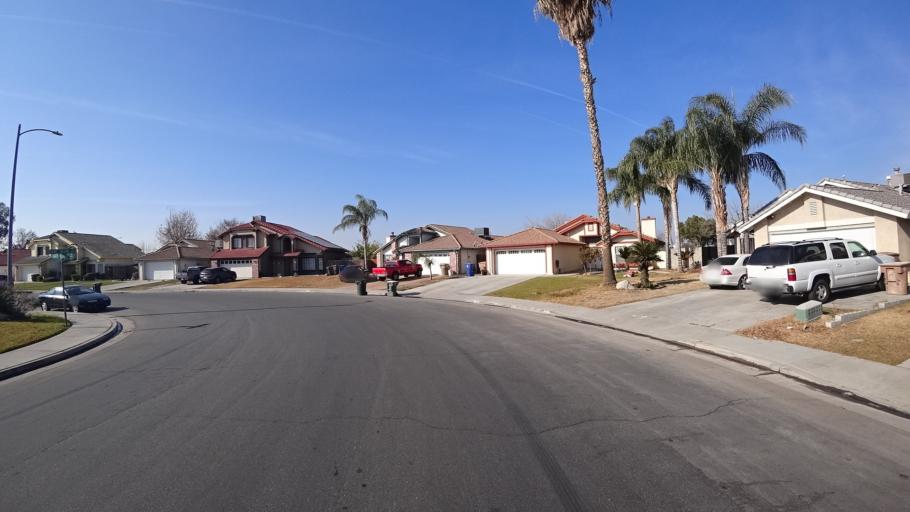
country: US
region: California
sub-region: Kern County
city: Greenfield
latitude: 35.3129
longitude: -119.0291
